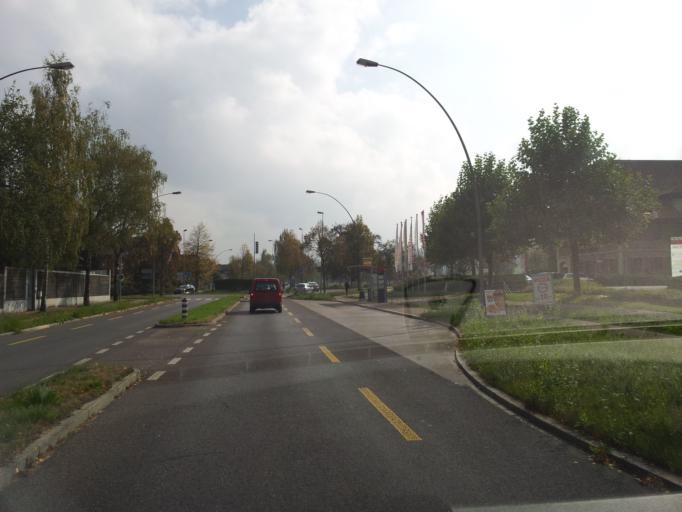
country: CH
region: Bern
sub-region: Bern-Mittelland District
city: Kehrsatz
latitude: 46.9234
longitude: 7.4601
